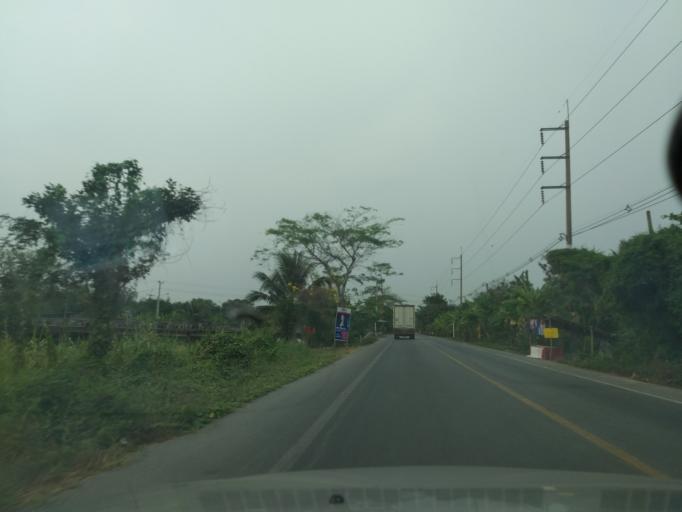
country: TH
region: Pathum Thani
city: Ban Lam Luk Ka
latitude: 13.9789
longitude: 100.8956
